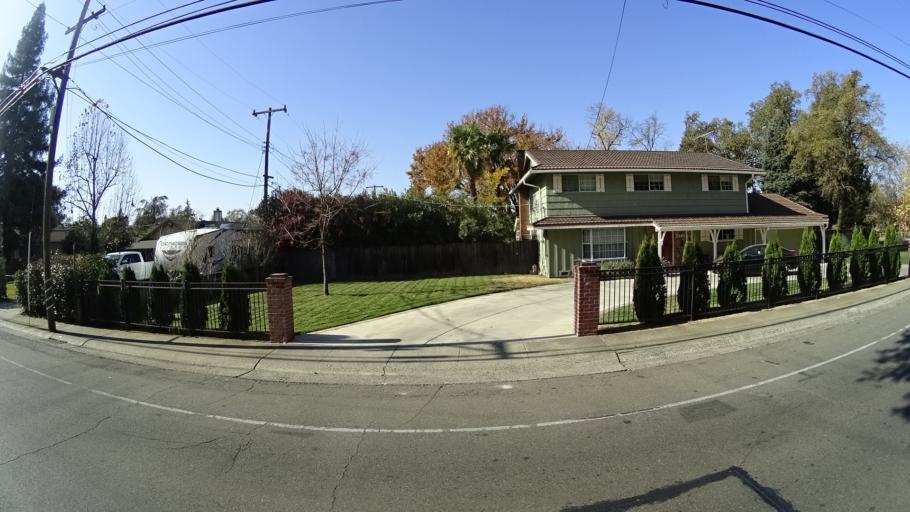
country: US
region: California
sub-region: Sacramento County
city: Citrus Heights
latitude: 38.6944
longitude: -121.2811
